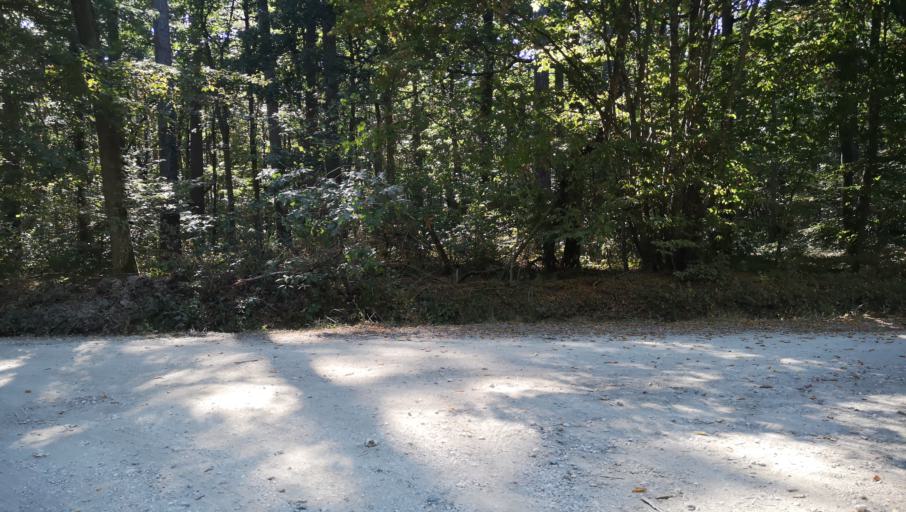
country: FR
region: Centre
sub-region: Departement du Loiret
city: Saran
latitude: 47.9610
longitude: 1.8958
